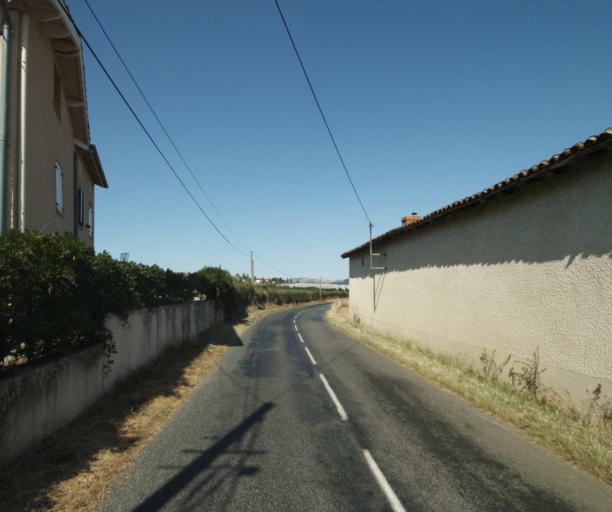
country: FR
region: Rhone-Alpes
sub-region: Departement du Rhone
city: Bessenay
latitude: 45.7695
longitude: 4.5447
